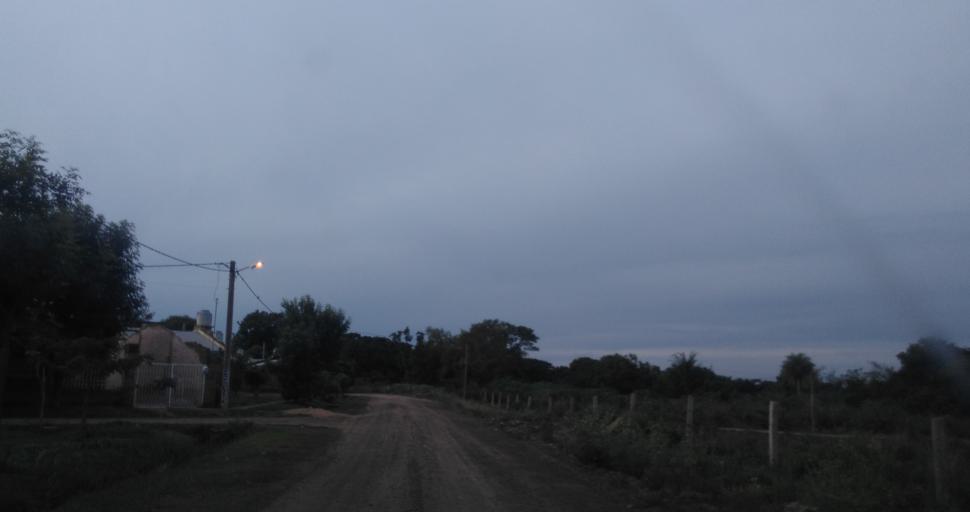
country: AR
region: Chaco
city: Fontana
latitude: -27.4114
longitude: -59.0252
